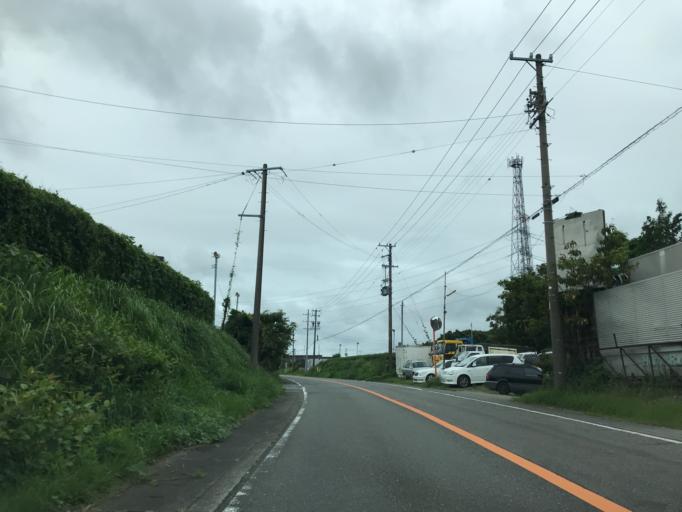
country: JP
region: Shizuoka
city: Kanaya
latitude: 34.7702
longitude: 138.1394
